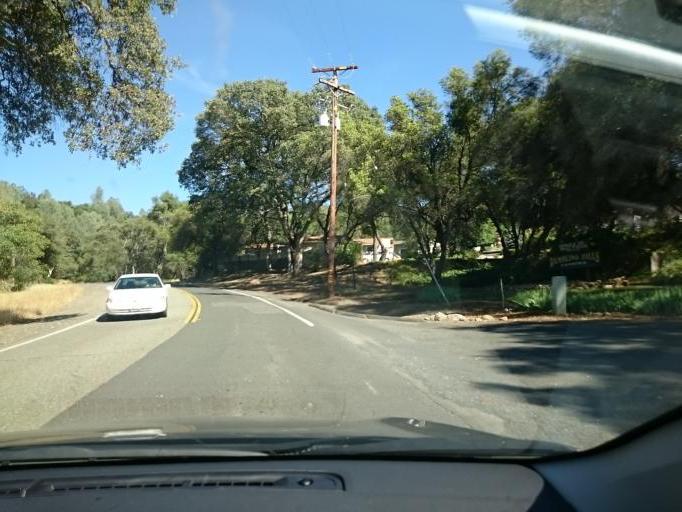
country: US
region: California
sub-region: Tuolumne County
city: Columbia
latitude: 38.0481
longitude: -120.4219
